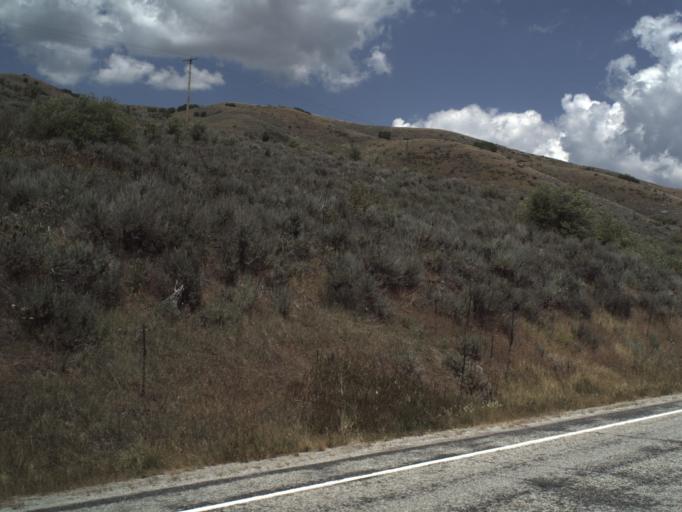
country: US
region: Utah
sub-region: Weber County
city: Wolf Creek
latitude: 41.2884
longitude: -111.6442
